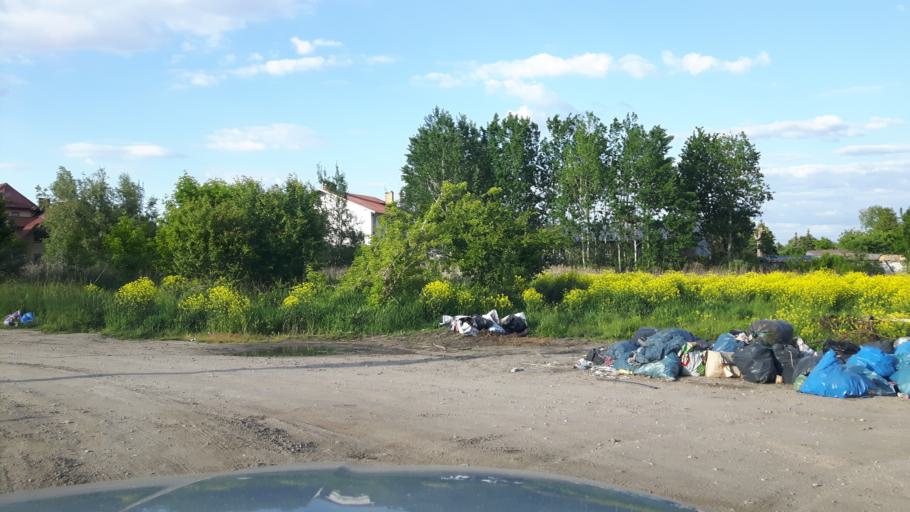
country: PL
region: Masovian Voivodeship
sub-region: Powiat wolominski
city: Zabki
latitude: 52.2851
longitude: 21.0878
